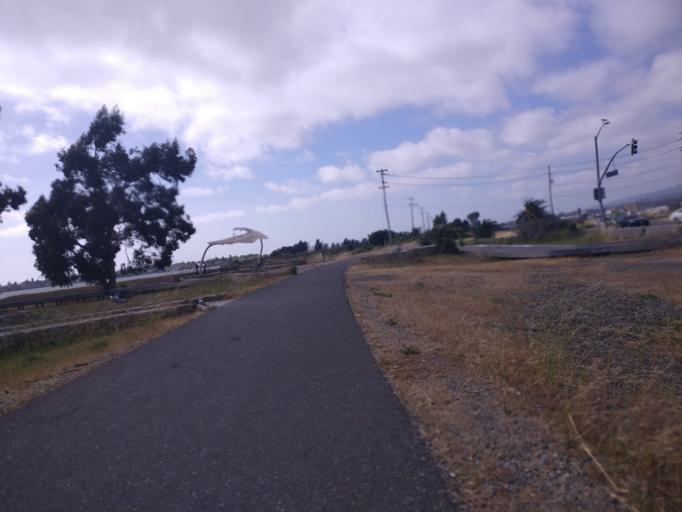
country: US
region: California
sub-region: Alameda County
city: Alameda
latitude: 37.7524
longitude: -122.2106
